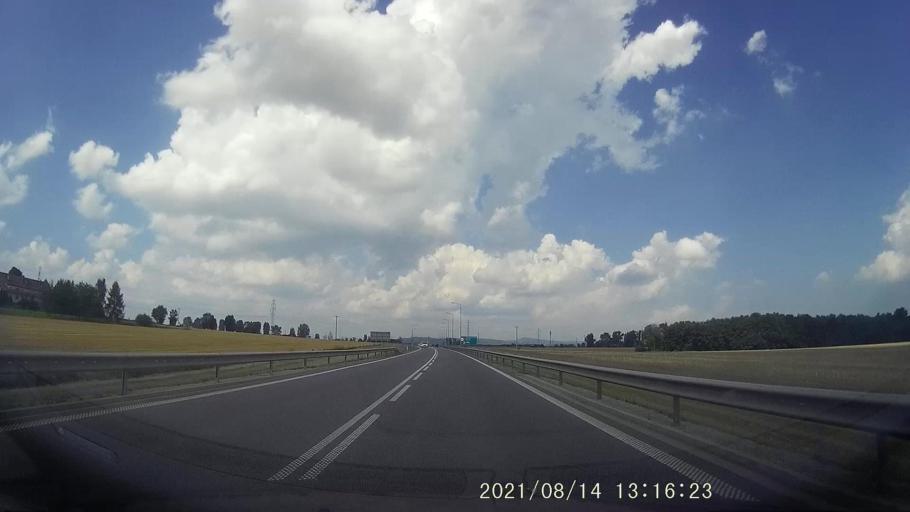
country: PL
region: Lower Silesian Voivodeship
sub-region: Powiat klodzki
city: Klodzko
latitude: 50.4316
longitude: 16.6287
